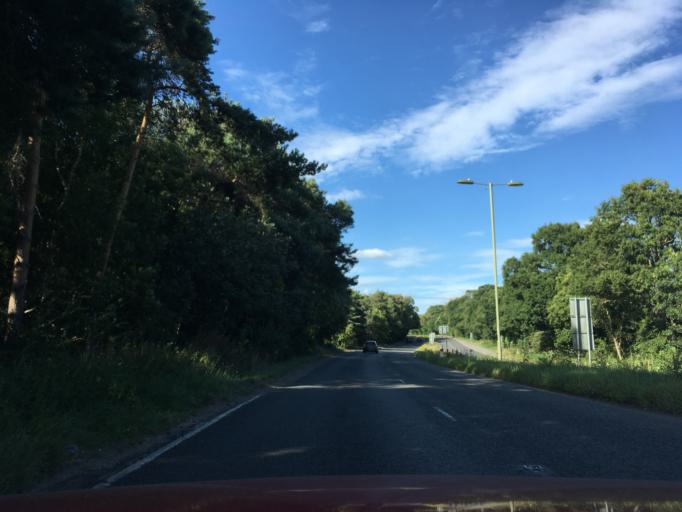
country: GB
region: England
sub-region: Hampshire
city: Romsey
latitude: 50.9547
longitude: -1.5340
